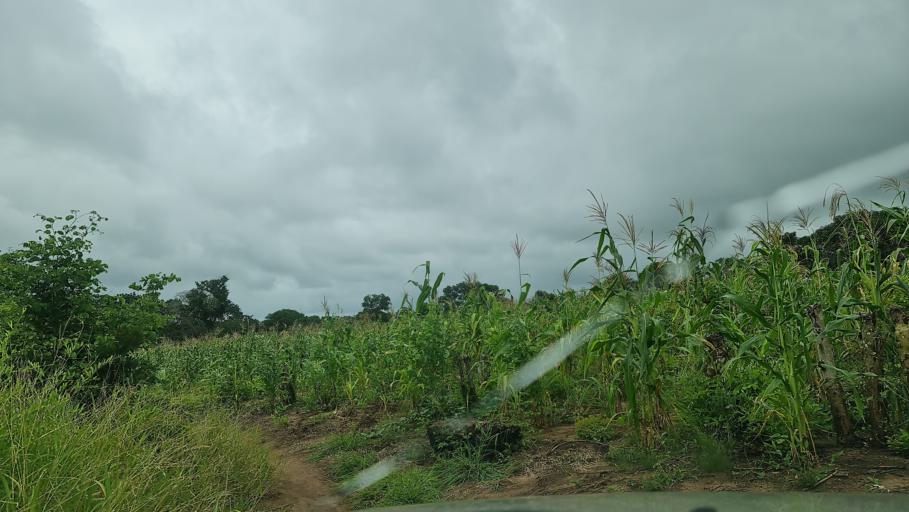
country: MW
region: Southern Region
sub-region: Nsanje District
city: Nsanje
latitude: -17.3975
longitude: 35.7868
